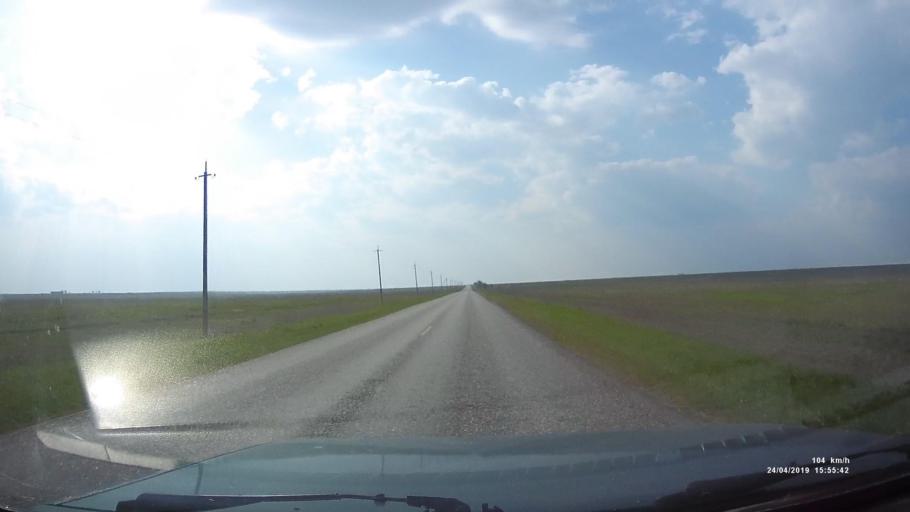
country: RU
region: Kalmykiya
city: Yashalta
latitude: 46.5924
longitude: 42.5438
